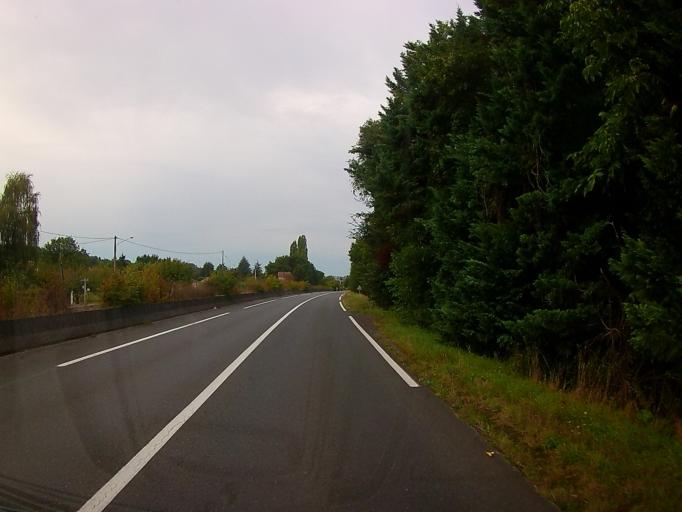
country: FR
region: Aquitaine
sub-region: Departement de la Dordogne
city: Annesse-et-Beaulieu
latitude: 45.1448
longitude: 0.5612
